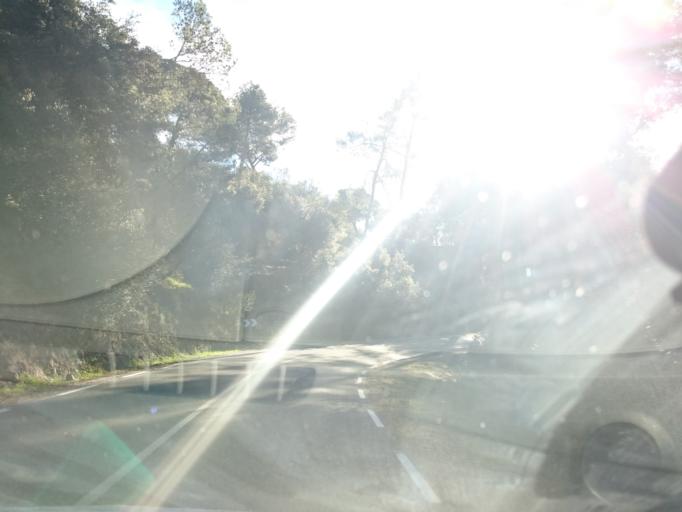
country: ES
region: Catalonia
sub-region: Provincia de Barcelona
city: Sant Just Desvern
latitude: 41.4079
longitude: 2.0932
